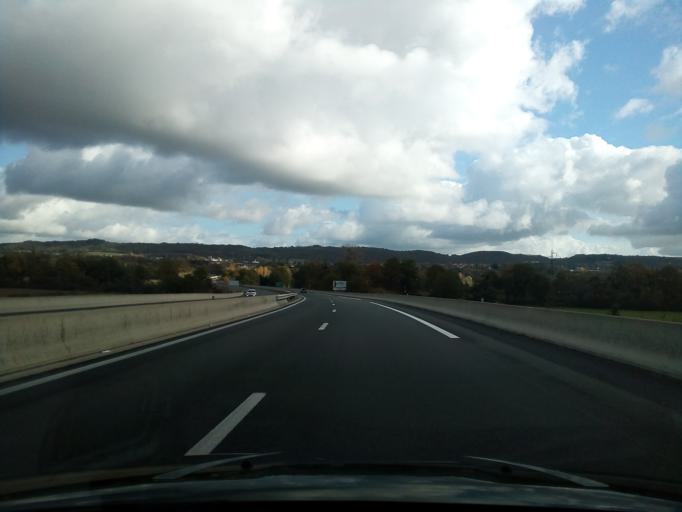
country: FR
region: Auvergne
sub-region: Departement de l'Allier
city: Saint-Victor
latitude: 46.3760
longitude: 2.5939
